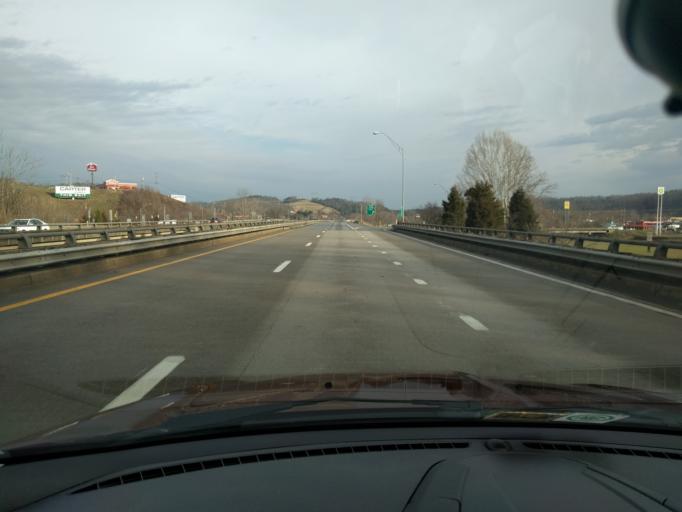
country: US
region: West Virginia
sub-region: Jackson County
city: Ripley
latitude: 38.8178
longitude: -81.7277
